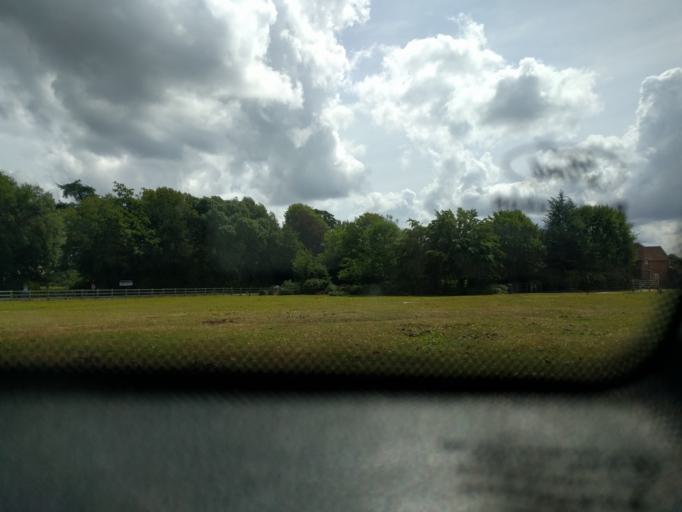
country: GB
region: England
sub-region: Hampshire
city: Brockenhurst
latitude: 50.8224
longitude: -1.5726
